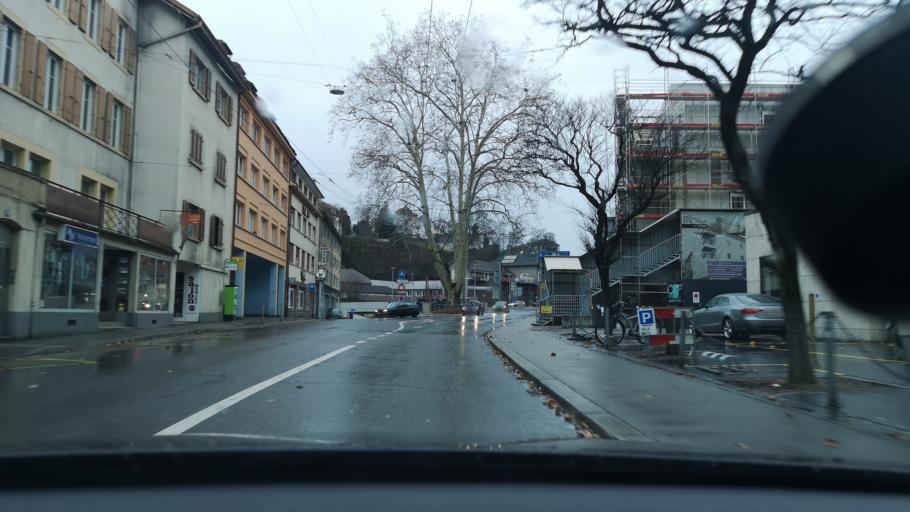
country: CH
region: Neuchatel
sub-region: Neuchatel District
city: Neuchatel
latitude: 46.9925
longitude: 6.9255
